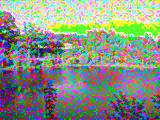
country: SE
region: Soedermanland
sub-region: Flens Kommun
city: Flen
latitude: 59.0675
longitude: 16.5910
